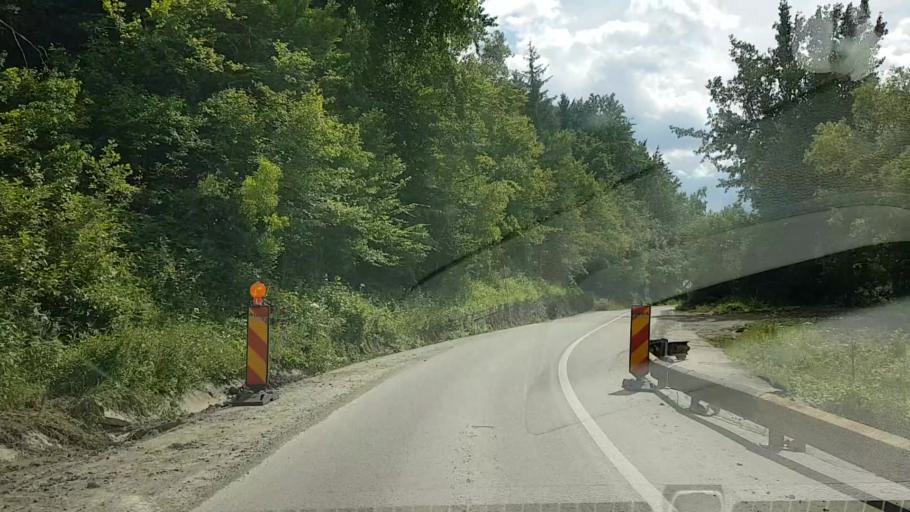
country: RO
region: Neamt
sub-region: Comuna Poiana Teiului
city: Poiana Teiului
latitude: 47.0789
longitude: 25.9681
